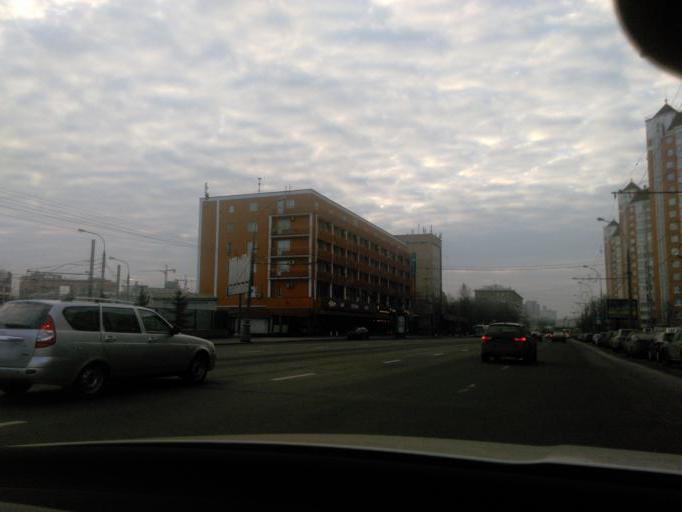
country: RU
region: Moskovskaya
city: Presnenskiy
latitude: 55.7686
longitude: 37.5572
